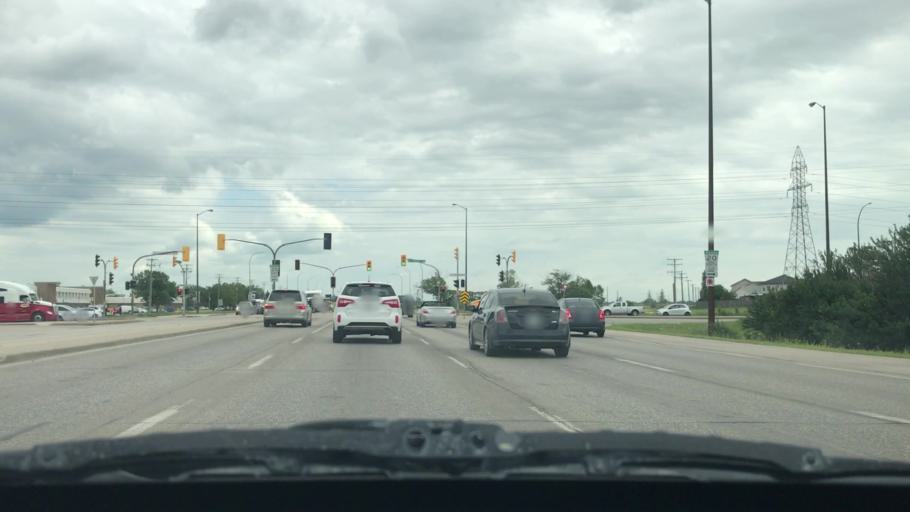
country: CA
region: Manitoba
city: Winnipeg
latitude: 49.8559
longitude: -97.0508
